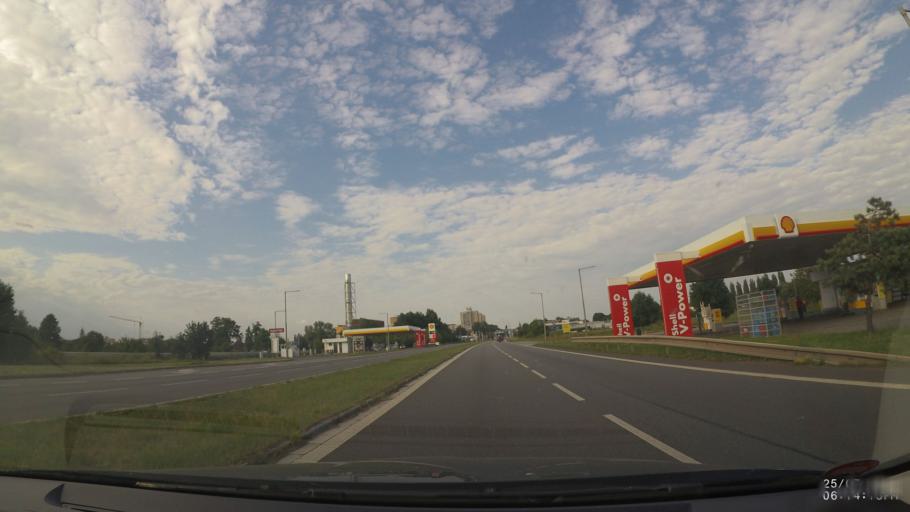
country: CZ
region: Kralovehradecky
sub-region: Okres Hradec Kralove
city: Hradec Kralove
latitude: 50.1934
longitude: 15.8104
